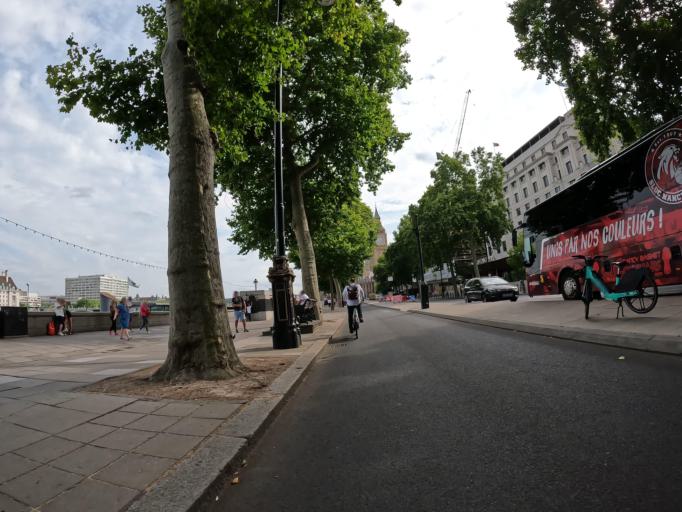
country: GB
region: England
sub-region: Greater London
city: Bromley
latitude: 51.4040
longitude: 0.0281
